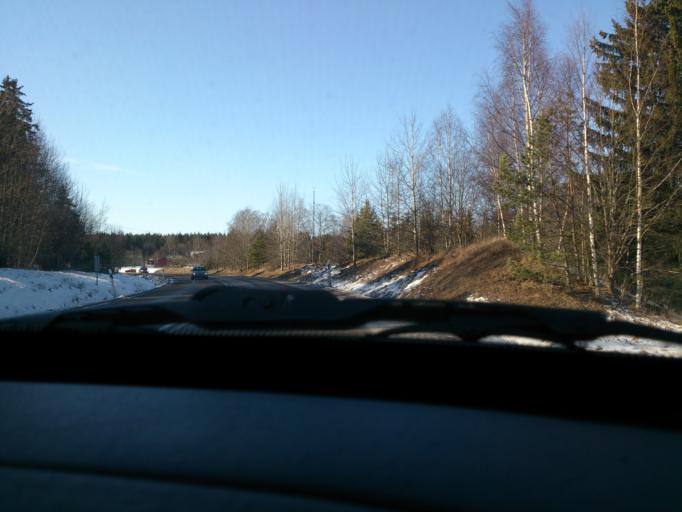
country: SE
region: Uppsala
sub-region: Uppsala Kommun
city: Saevja
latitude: 59.8579
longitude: 17.8111
